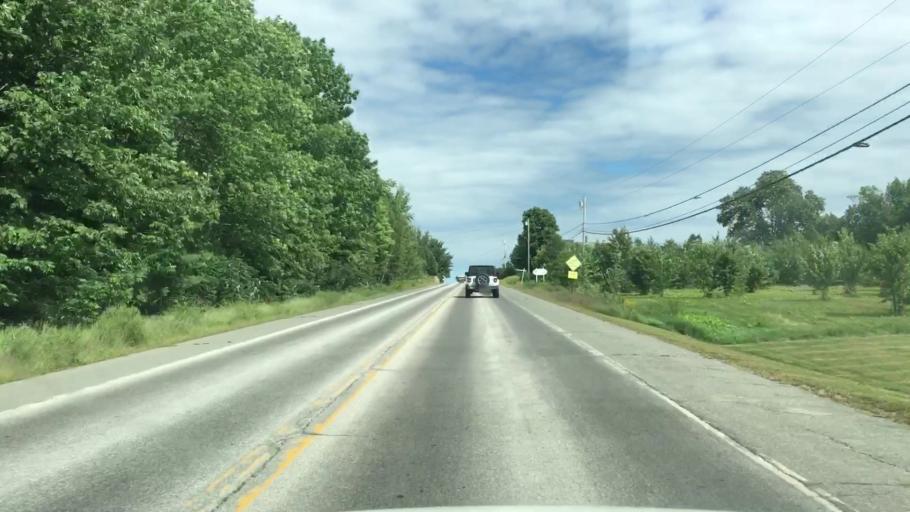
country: US
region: Maine
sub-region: Piscataquis County
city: Dover-Foxcroft
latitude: 45.1614
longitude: -69.2319
